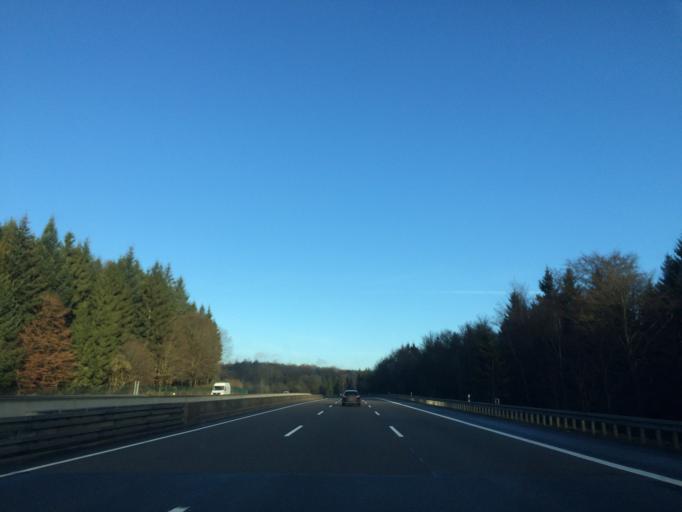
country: DE
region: Hesse
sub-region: Regierungsbezirk Kassel
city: Kirchheim
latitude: 50.8778
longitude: 9.6010
